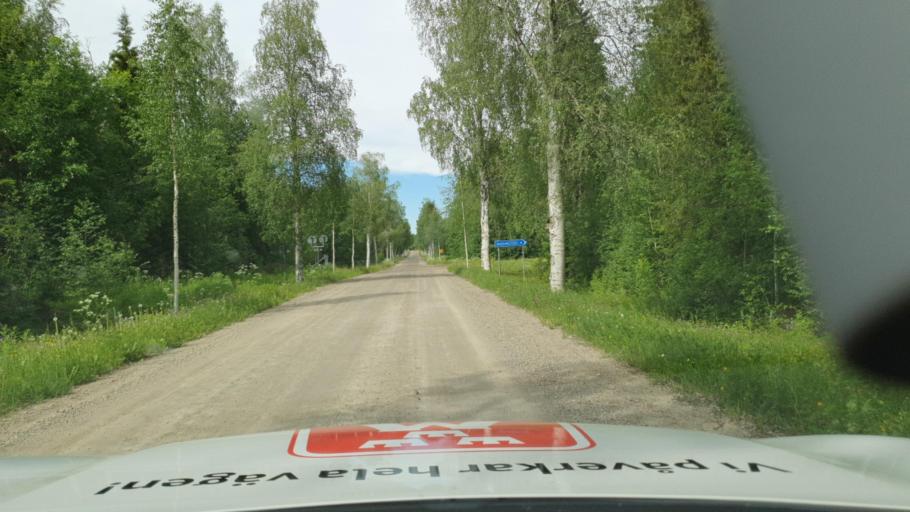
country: SE
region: Vaesterbotten
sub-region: Skelleftea Kommun
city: Burtraesk
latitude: 64.4632
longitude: 20.4657
